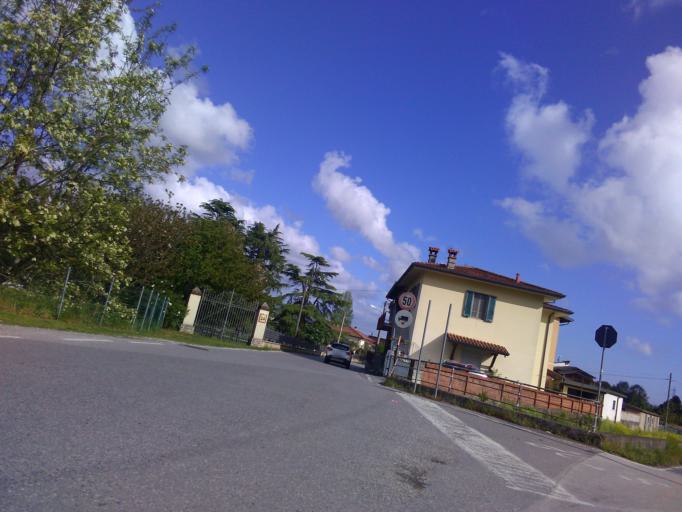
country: IT
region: Tuscany
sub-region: Provincia di Massa-Carrara
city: Capanne-Prato-Cinquale
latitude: 44.0078
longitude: 10.1473
